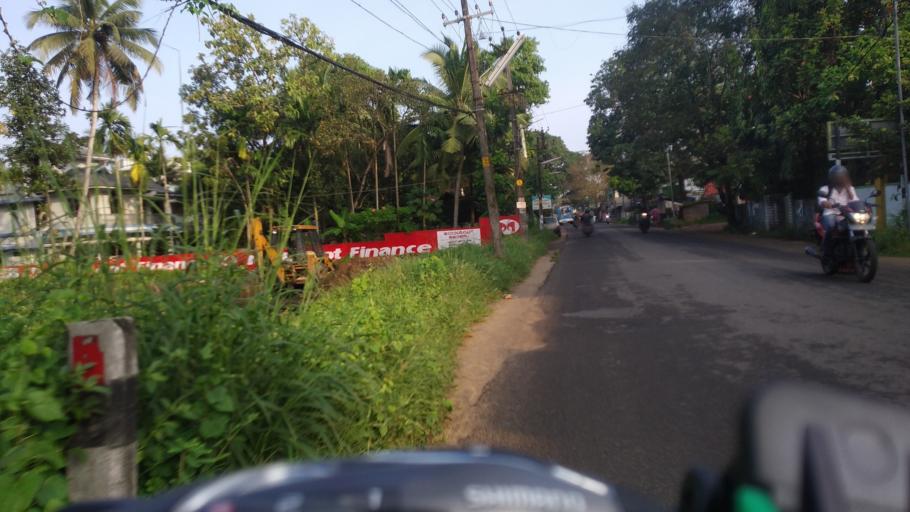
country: IN
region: Kerala
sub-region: Ernakulam
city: Elur
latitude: 10.0772
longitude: 76.2109
